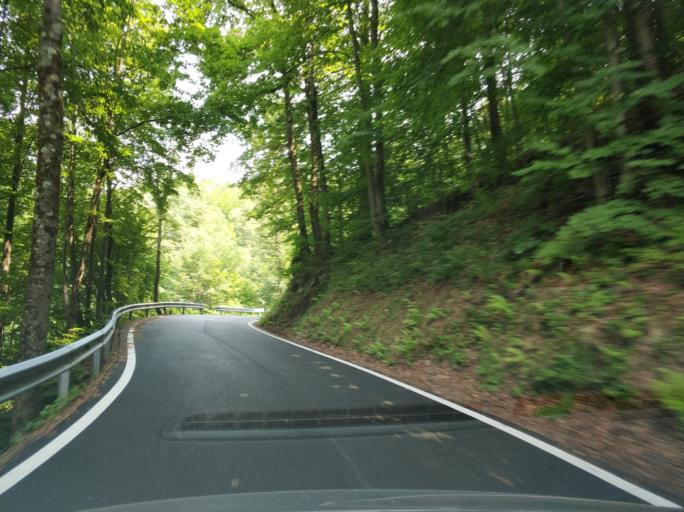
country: IT
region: Piedmont
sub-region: Provincia di Torino
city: Viu
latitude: 45.2306
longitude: 7.3705
